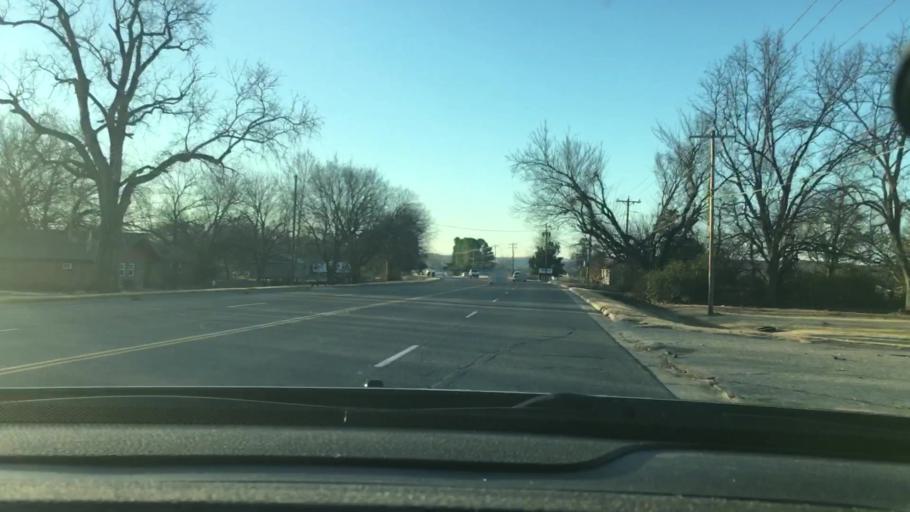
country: US
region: Oklahoma
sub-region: Murray County
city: Davis
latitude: 34.4760
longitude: -97.1317
